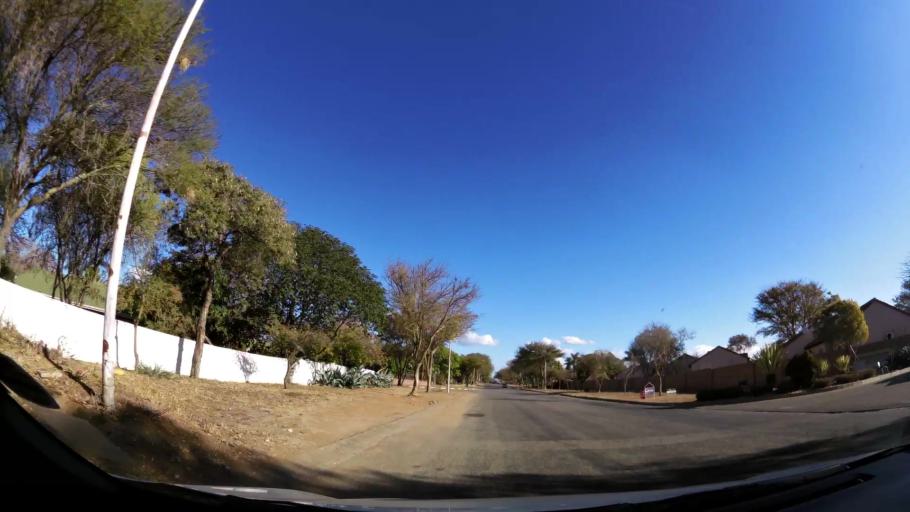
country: ZA
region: Limpopo
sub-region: Capricorn District Municipality
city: Polokwane
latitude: -23.8871
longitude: 29.4873
